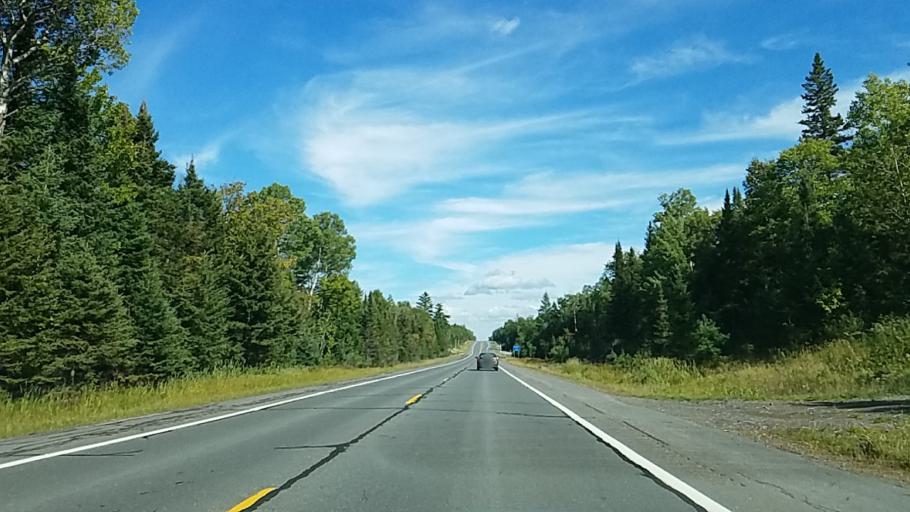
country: US
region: Michigan
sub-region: Baraga County
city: L'Anse
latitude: 46.5759
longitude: -88.3449
